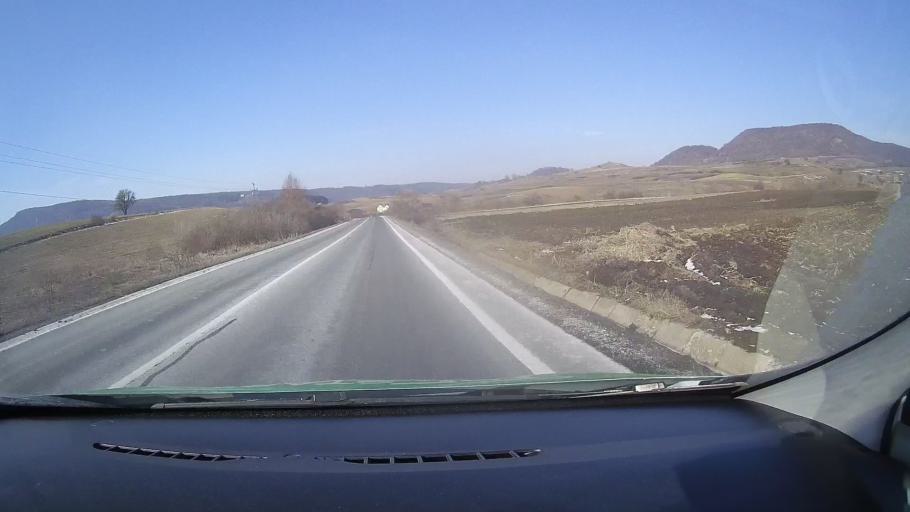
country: RO
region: Mures
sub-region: Comuna Saschiz
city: Saschiz
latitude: 46.1793
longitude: 24.9769
